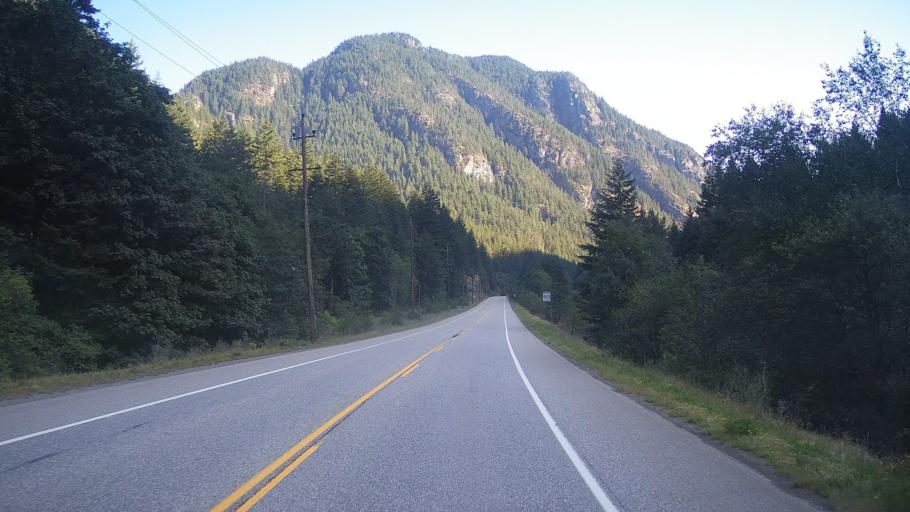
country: CA
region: British Columbia
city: Hope
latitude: 49.6022
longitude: -121.4158
